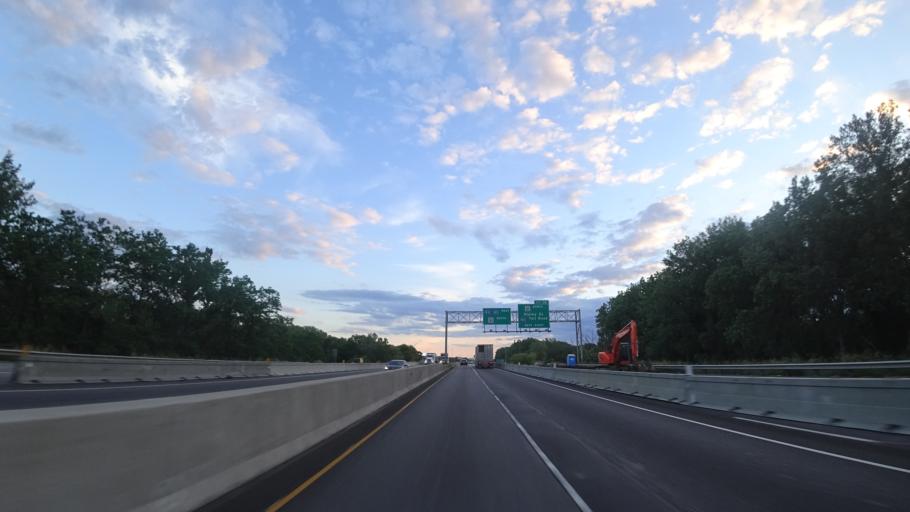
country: US
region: Indiana
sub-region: Lake County
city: Lake Station
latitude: 41.5910
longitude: -87.2226
